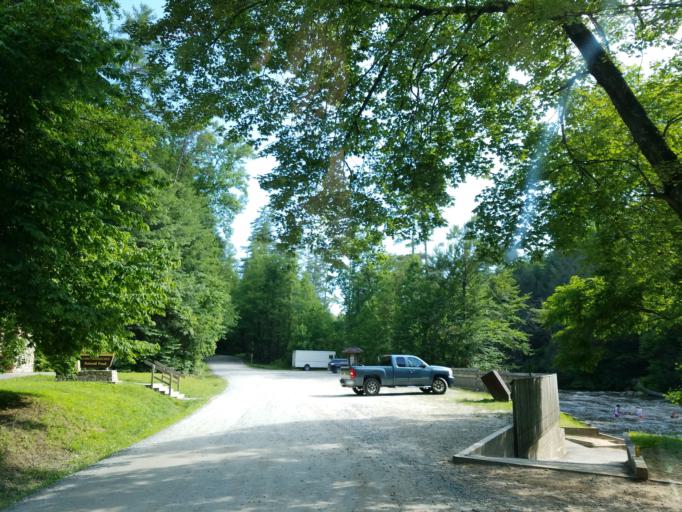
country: US
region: Georgia
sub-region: Fannin County
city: Blue Ridge
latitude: 34.7864
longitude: -84.2397
